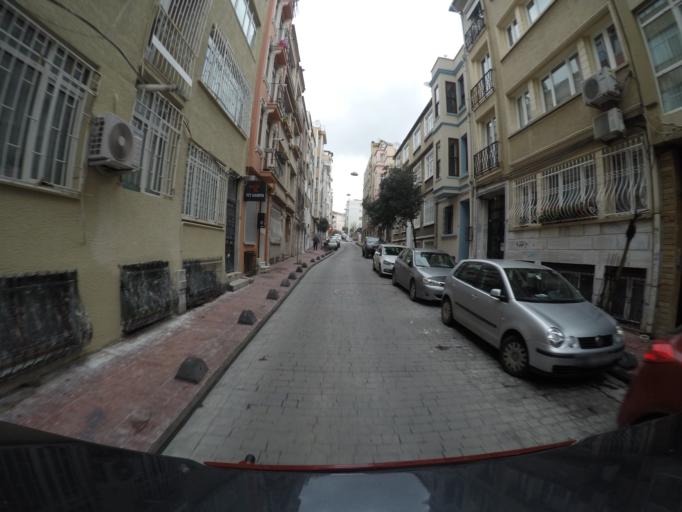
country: TR
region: Istanbul
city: Eminoenue
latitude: 41.0308
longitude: 28.9861
